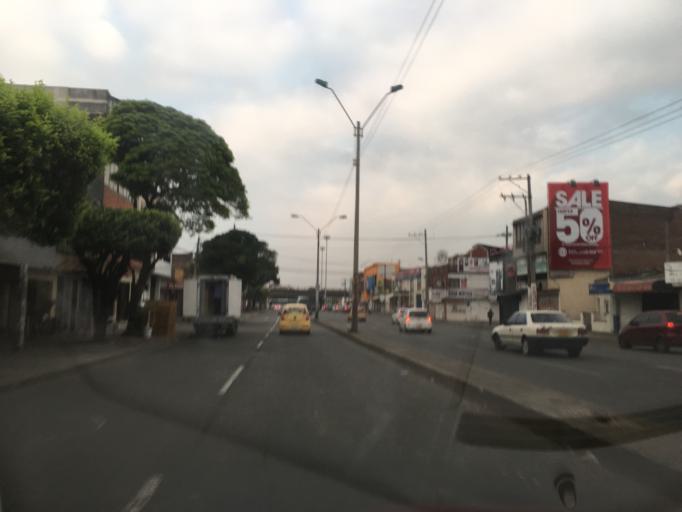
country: CO
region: Valle del Cauca
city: Cali
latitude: 3.4375
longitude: -76.5199
